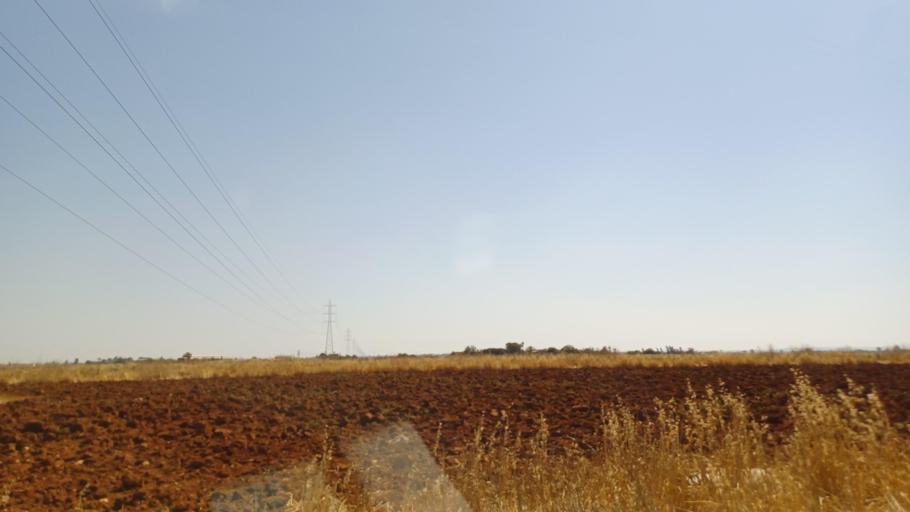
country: CY
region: Ammochostos
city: Avgorou
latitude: 35.0108
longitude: 33.8141
